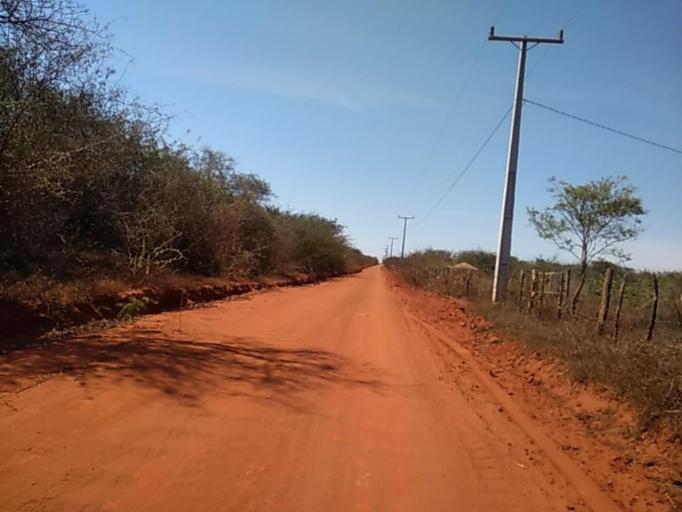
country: BR
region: Bahia
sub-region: Caetite
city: Caetite
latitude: -13.9835
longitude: -42.5105
